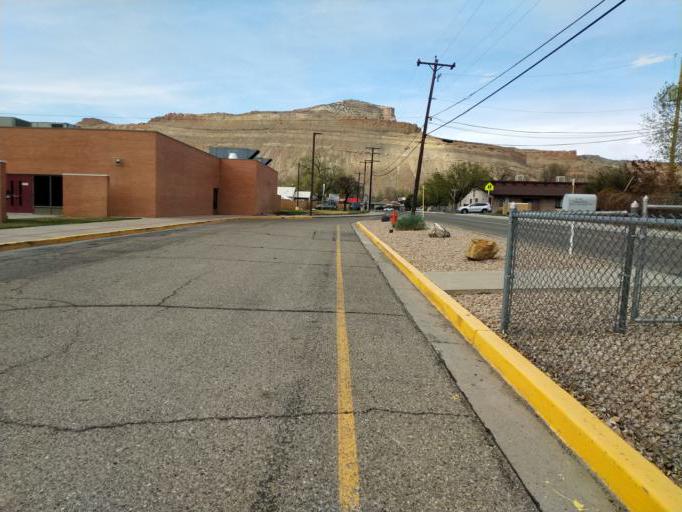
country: US
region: Colorado
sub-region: Mesa County
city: Palisade
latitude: 39.1043
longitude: -108.3528
